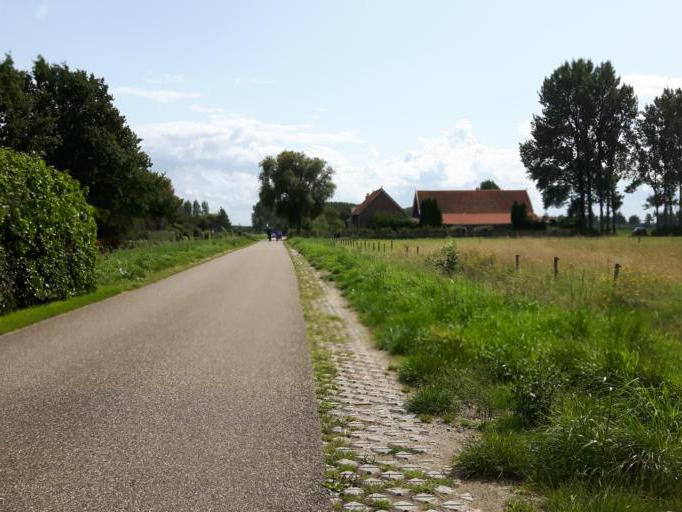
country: NL
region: Zeeland
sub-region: Gemeente Borsele
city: Borssele
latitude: 51.4692
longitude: 3.8056
